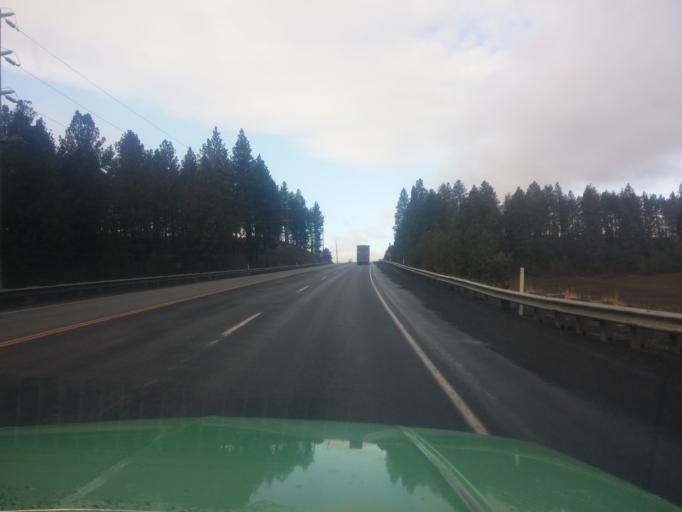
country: US
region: Idaho
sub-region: Latah County
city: Moscow
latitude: 46.9106
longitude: -116.9547
